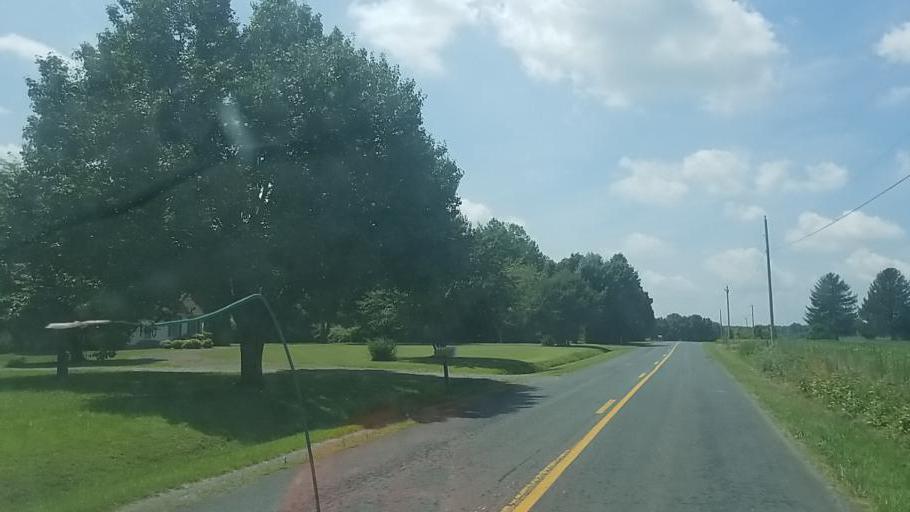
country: US
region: Maryland
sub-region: Talbot County
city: Easton
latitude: 38.7777
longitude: -76.0128
